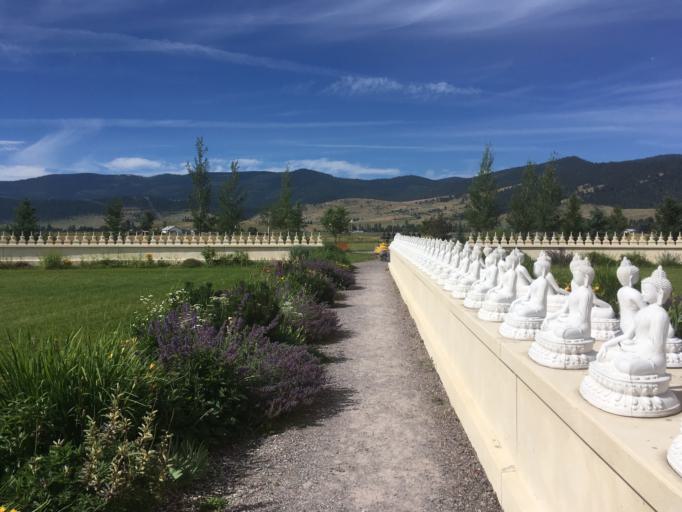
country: US
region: Montana
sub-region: Missoula County
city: Frenchtown
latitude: 47.1915
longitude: -114.0900
